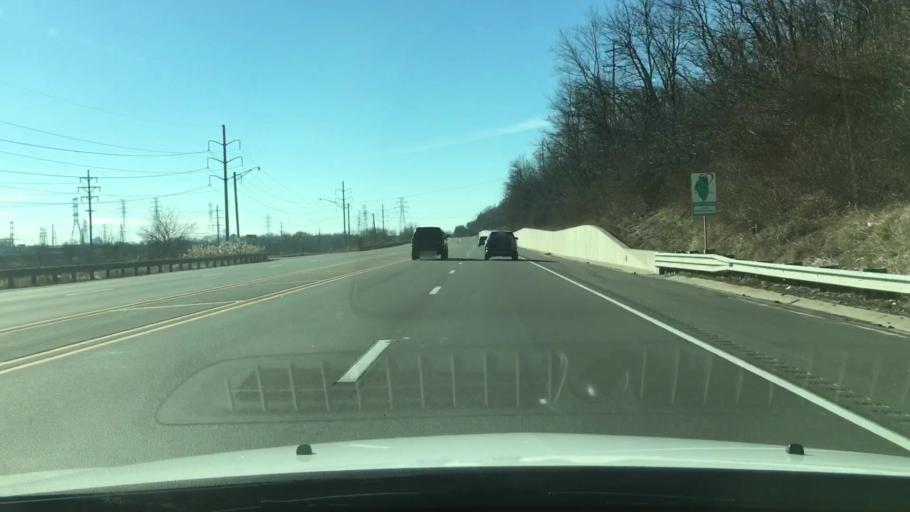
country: US
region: Illinois
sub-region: Tazewell County
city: North Pekin
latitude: 40.6059
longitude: -89.6636
